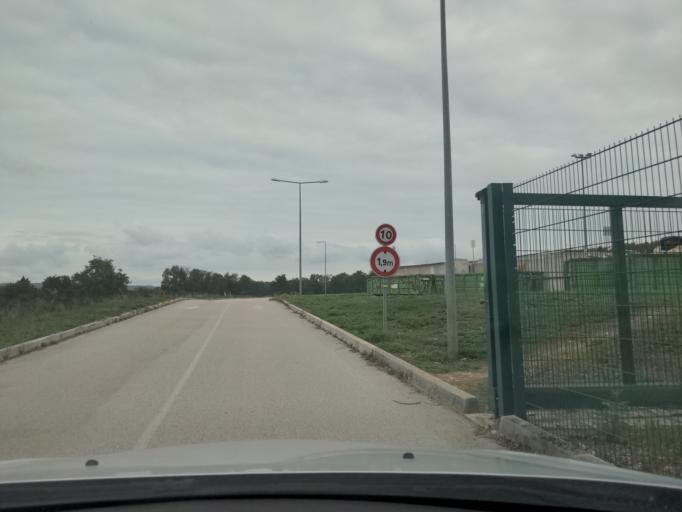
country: FR
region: Bourgogne
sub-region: Departement de la Cote-d'Or
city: Ahuy
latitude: 47.3652
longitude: 5.0384
